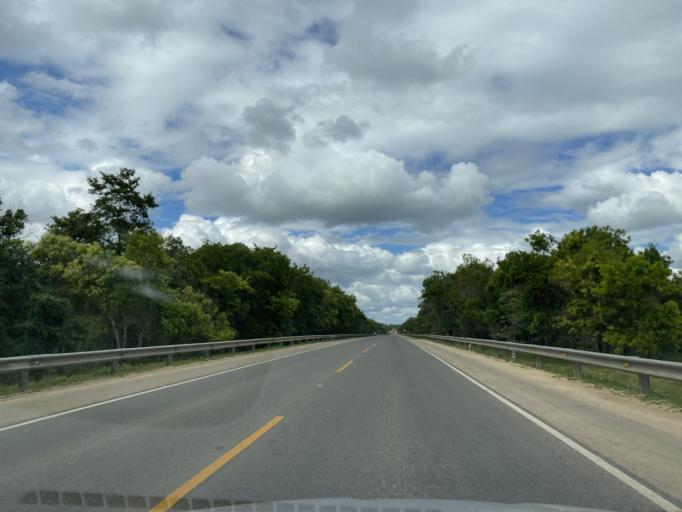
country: DO
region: Santo Domingo
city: Guerra
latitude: 18.5365
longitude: -69.7553
